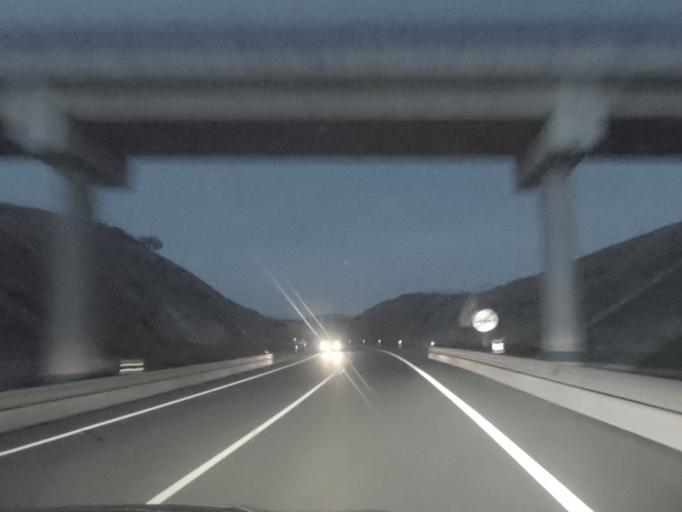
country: PT
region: Braganca
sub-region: Mogadouro
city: Mogadouro
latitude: 41.2604
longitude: -6.7872
